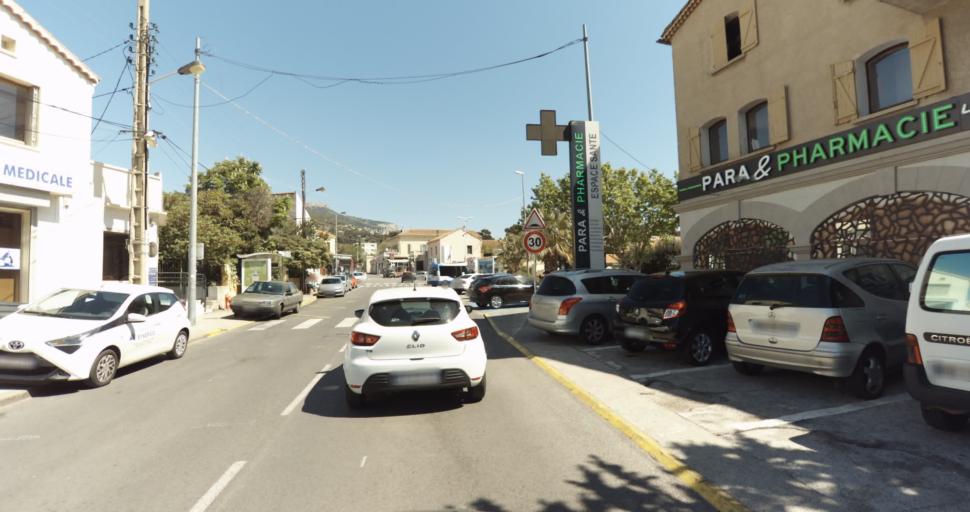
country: FR
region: Provence-Alpes-Cote d'Azur
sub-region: Departement du Var
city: Le Revest-les-Eaux
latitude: 43.1465
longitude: 5.9020
